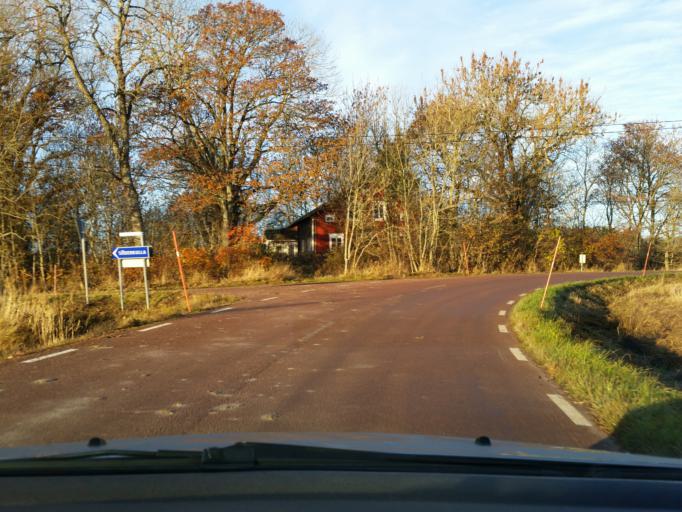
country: AX
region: Alands landsbygd
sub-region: Saltvik
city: Saltvik
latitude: 60.2737
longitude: 20.0762
